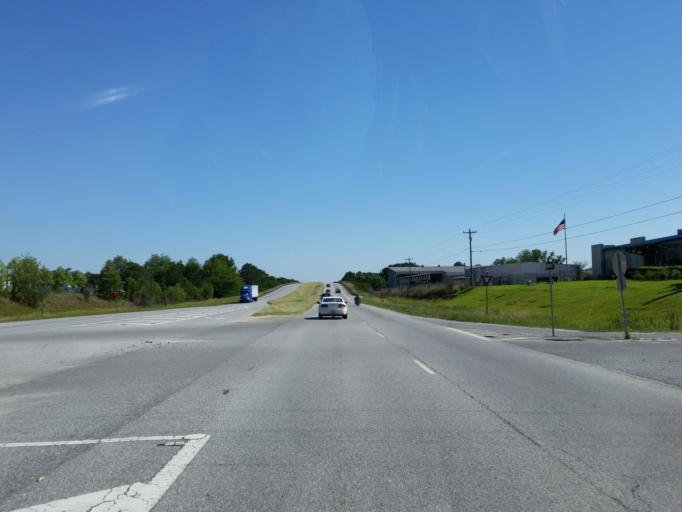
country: US
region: Georgia
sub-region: Lowndes County
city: Valdosta
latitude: 30.8357
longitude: -83.2281
